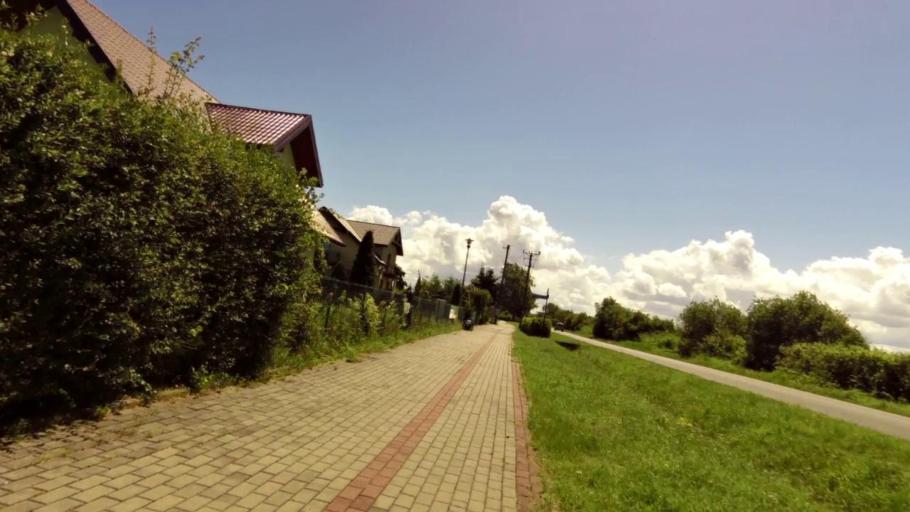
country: PL
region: West Pomeranian Voivodeship
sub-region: Koszalin
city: Koszalin
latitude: 54.3032
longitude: 16.2007
